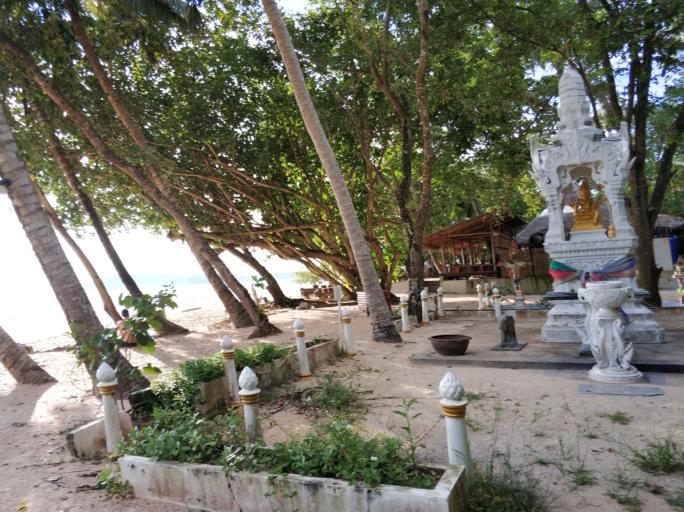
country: TH
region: Phangnga
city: Ban Ao Nang
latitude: 8.0271
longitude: 98.8267
